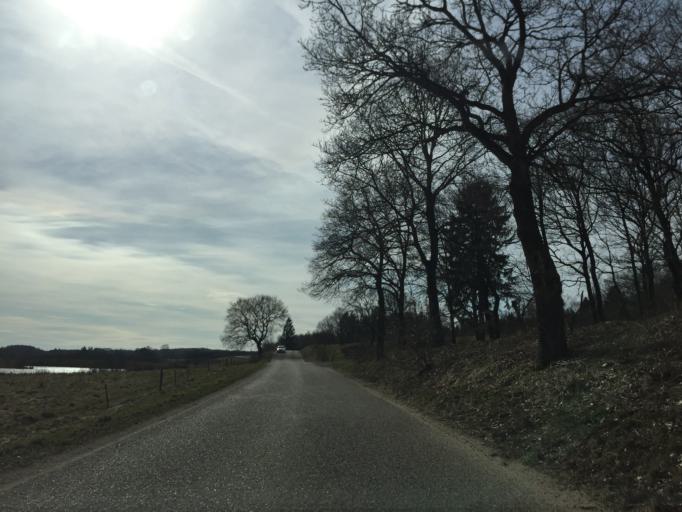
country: DK
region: Central Jutland
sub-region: Silkeborg Kommune
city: Svejbaek
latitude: 56.2005
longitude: 9.6461
